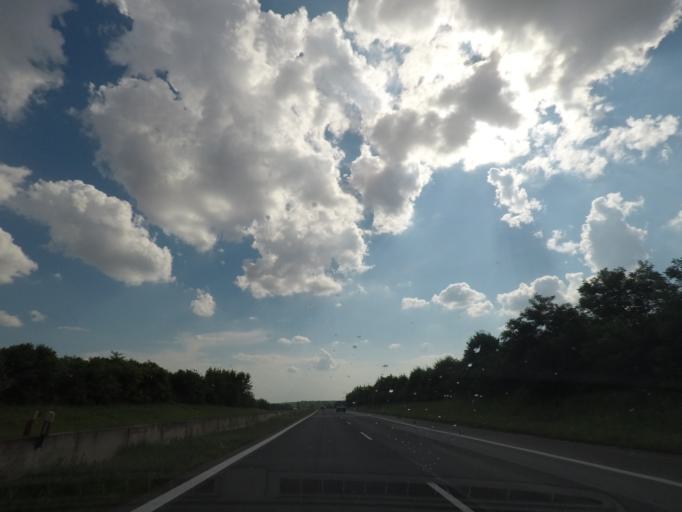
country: PL
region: Silesian Voivodeship
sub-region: Powiat czestochowski
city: Borowno
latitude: 50.9552
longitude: 19.2468
